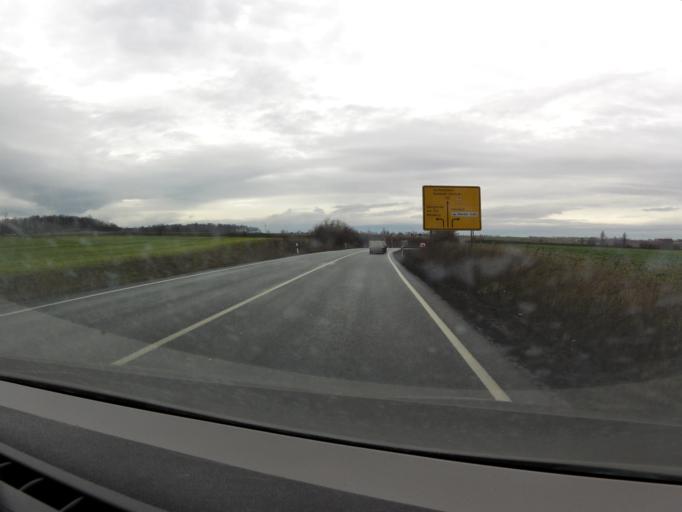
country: DE
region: Saxony-Anhalt
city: Grossorner
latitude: 51.6373
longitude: 11.4763
